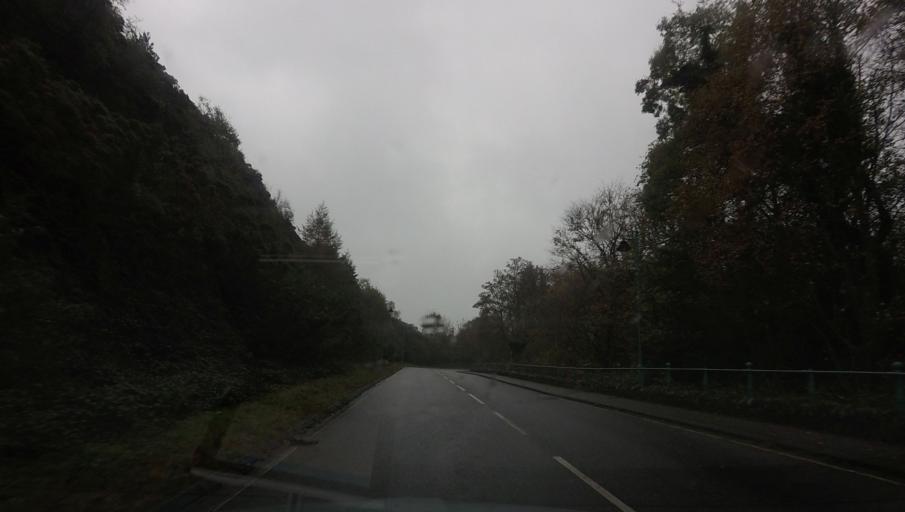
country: GB
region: Scotland
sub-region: Argyll and Bute
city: Isle Of Mull
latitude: 56.6200
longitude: -6.0709
